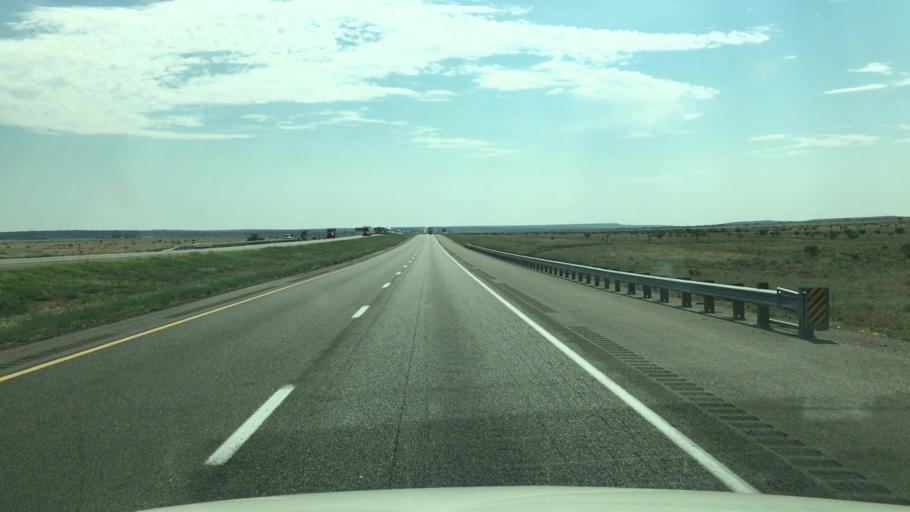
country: US
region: New Mexico
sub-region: Guadalupe County
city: Santa Rosa
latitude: 34.9779
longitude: -105.0224
